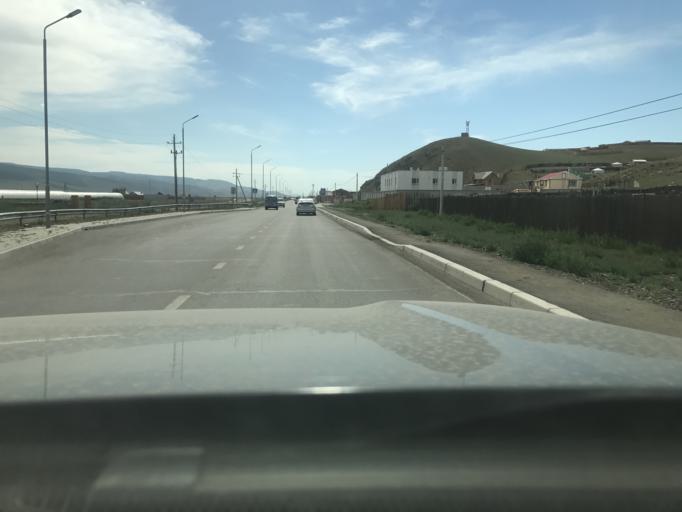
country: MN
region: Ulaanbaatar
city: Ulaanbaatar
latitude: 47.9166
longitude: 107.1047
